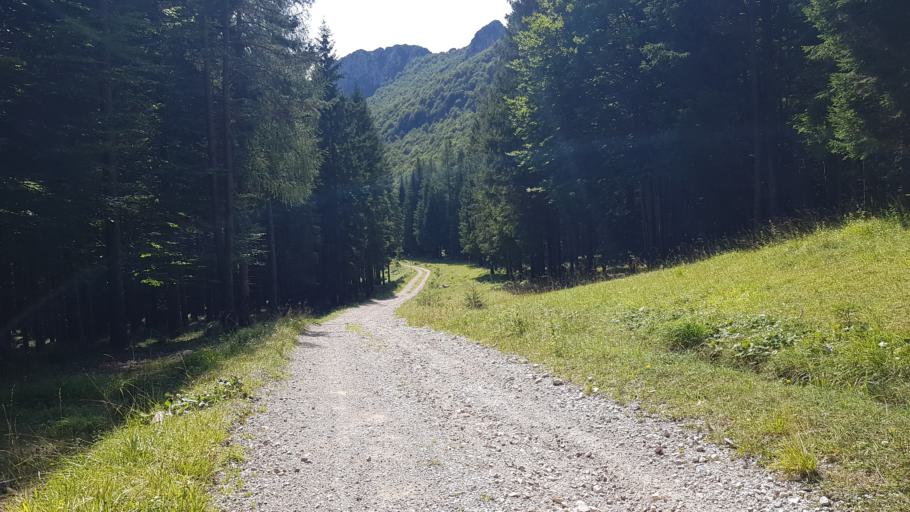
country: IT
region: Friuli Venezia Giulia
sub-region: Provincia di Udine
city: Moggio Udinese
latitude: 46.4617
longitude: 13.2217
